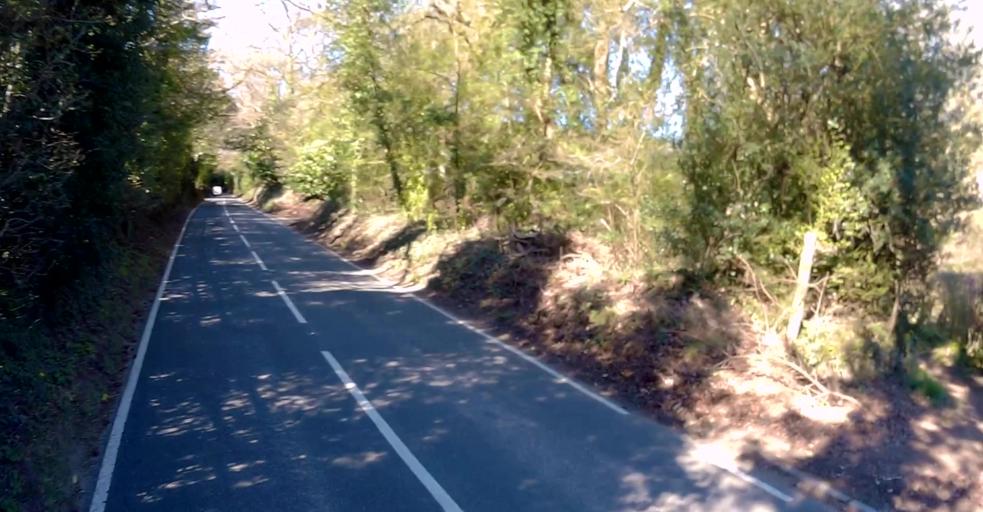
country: GB
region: England
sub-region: Surrey
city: Farnham
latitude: 51.2029
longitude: -0.7779
